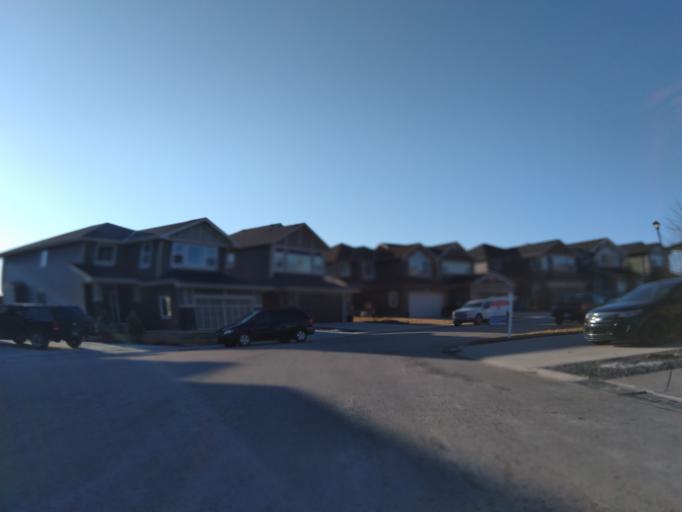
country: CA
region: Alberta
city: Cochrane
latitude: 51.1826
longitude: -114.5053
